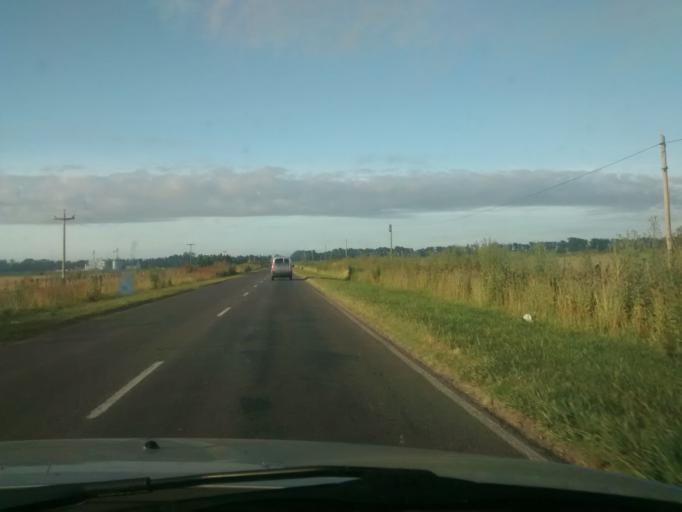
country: AR
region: Buenos Aires
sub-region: Partido de Brandsen
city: Brandsen
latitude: -35.1204
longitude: -58.1872
